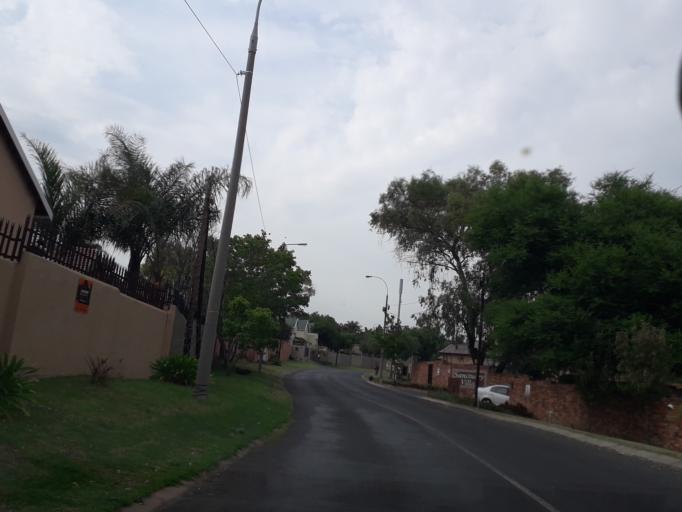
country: ZA
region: Gauteng
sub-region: City of Johannesburg Metropolitan Municipality
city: Roodepoort
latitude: -26.1012
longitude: 27.9217
